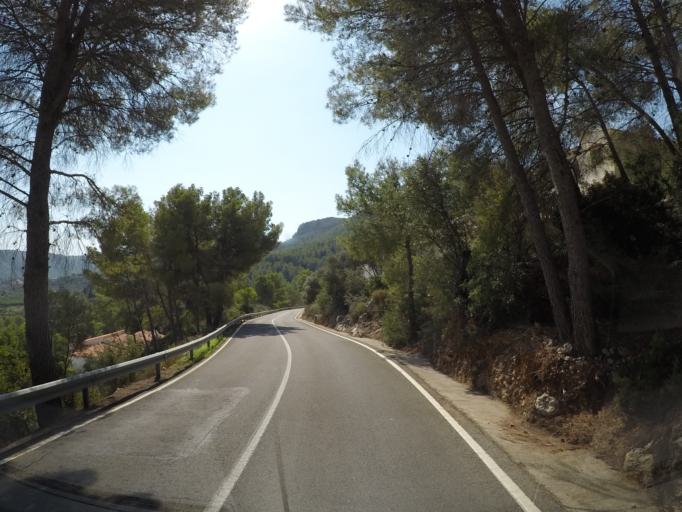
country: ES
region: Valencia
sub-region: Provincia de Alicante
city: Orba
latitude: 38.7824
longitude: -0.0799
